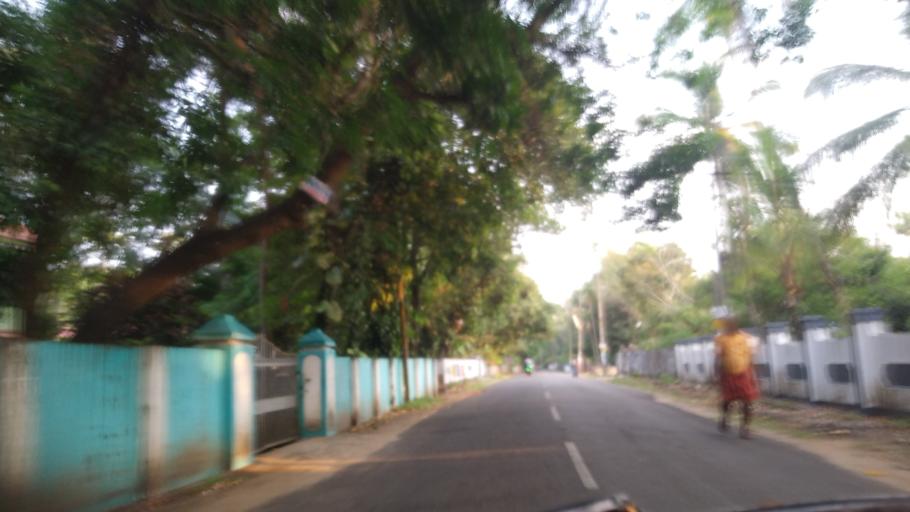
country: IN
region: Kerala
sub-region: Thrissur District
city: Thanniyam
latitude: 10.3490
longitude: 76.1137
